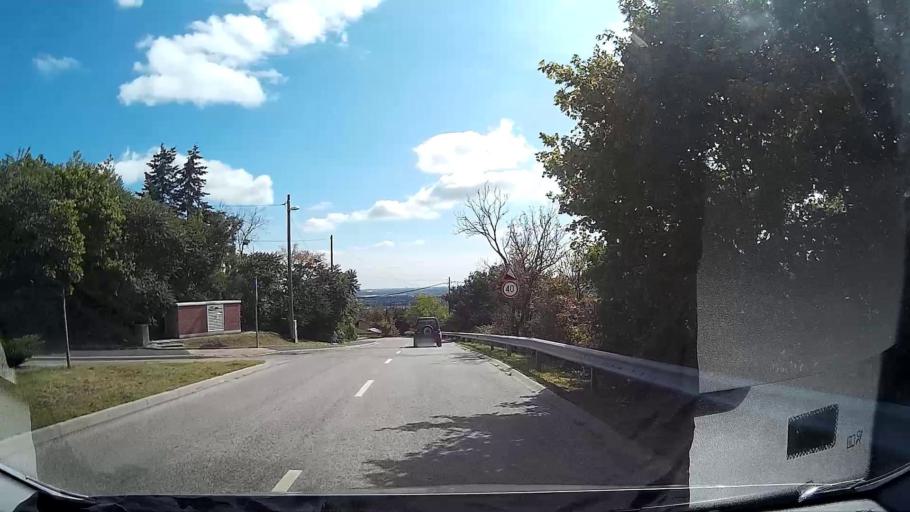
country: HU
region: Pest
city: Szentendre
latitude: 47.6950
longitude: 19.0612
